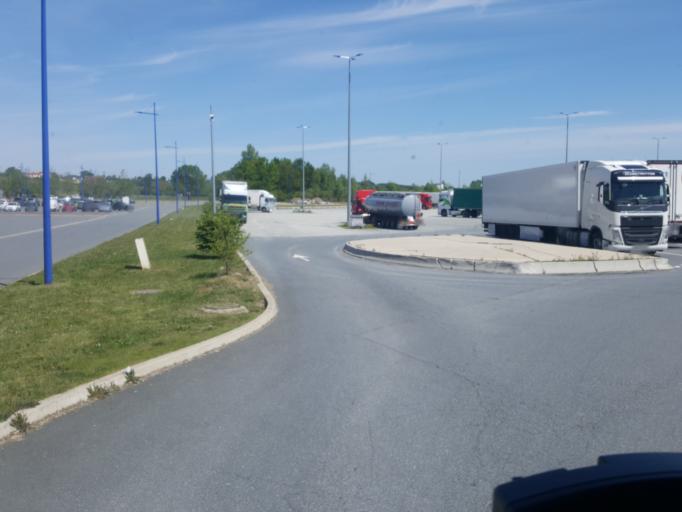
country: FR
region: Auvergne
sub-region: Departement de l'Allier
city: Saint-Victor
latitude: 46.3784
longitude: 2.5851
